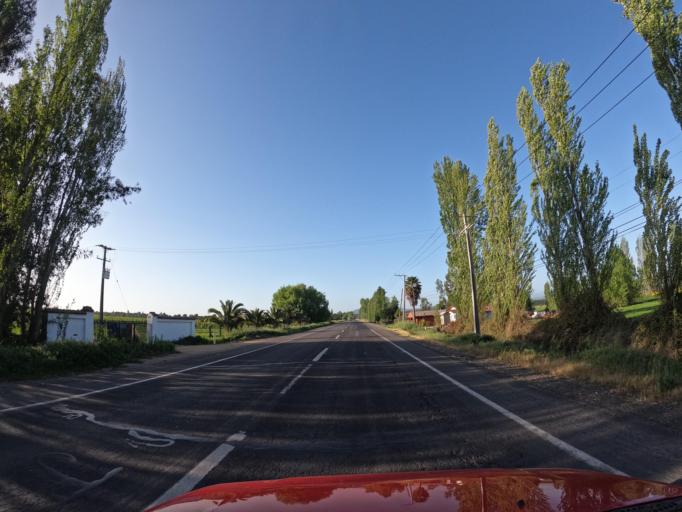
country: CL
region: O'Higgins
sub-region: Provincia de Colchagua
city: Santa Cruz
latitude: -34.4839
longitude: -71.3604
